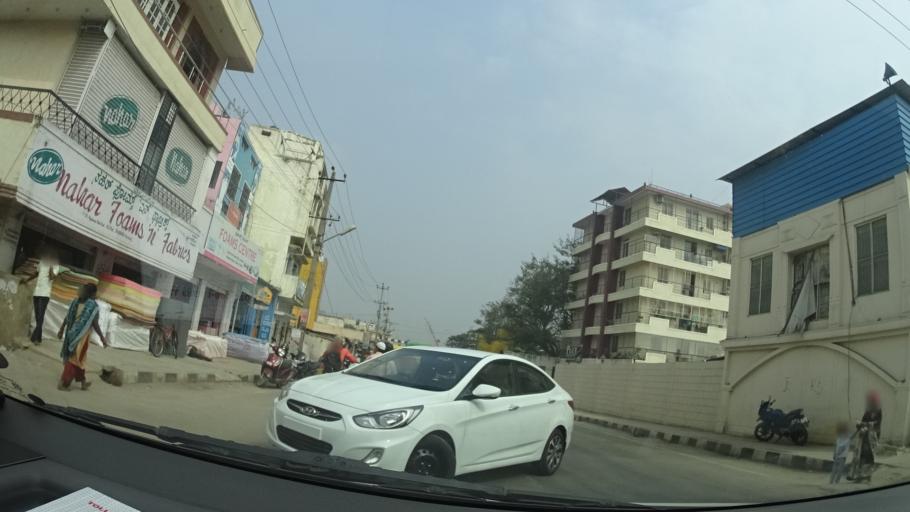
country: IN
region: Karnataka
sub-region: Bangalore Urban
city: Bangalore
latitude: 13.0253
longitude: 77.6197
